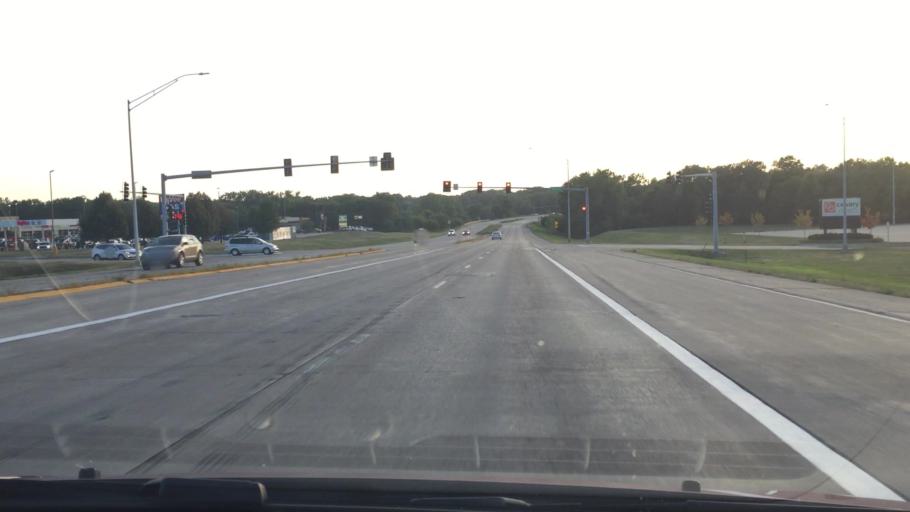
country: US
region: Iowa
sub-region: Muscatine County
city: Muscatine
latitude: 41.4530
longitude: -91.0339
